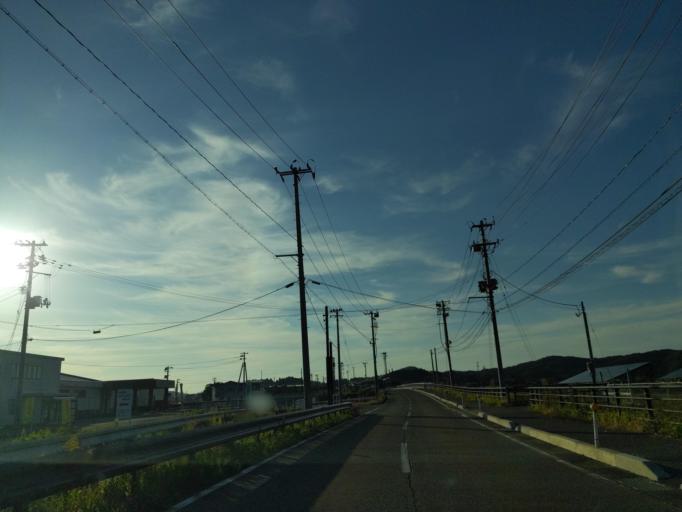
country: JP
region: Niigata
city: Yoshida-kasugacho
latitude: 37.5805
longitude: 138.7789
